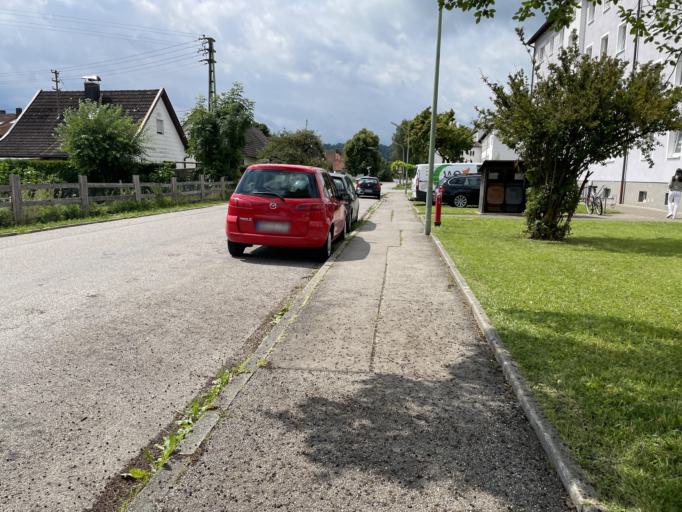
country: DE
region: Bavaria
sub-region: Upper Bavaria
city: Peissenberg
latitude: 47.7900
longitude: 11.0655
